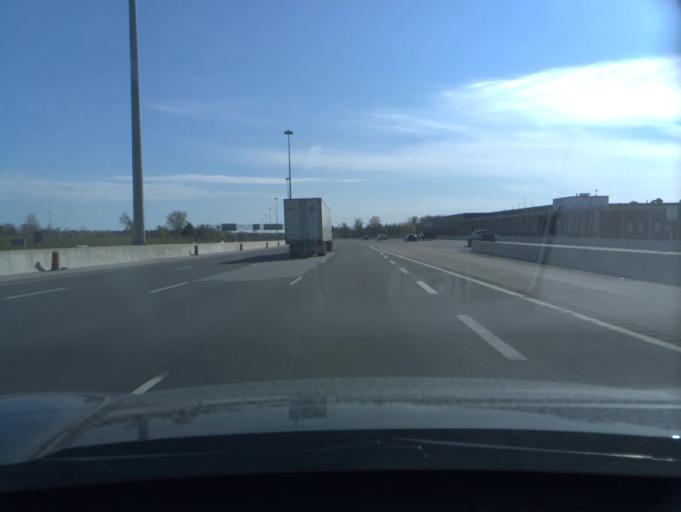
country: CA
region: Ontario
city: North Perth
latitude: 43.8105
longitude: -80.9996
